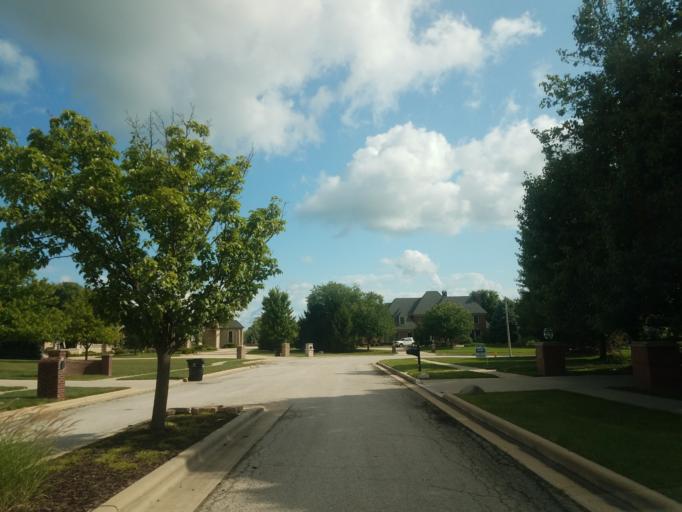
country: US
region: Illinois
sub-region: McLean County
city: Normal
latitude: 40.5084
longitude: -88.9111
